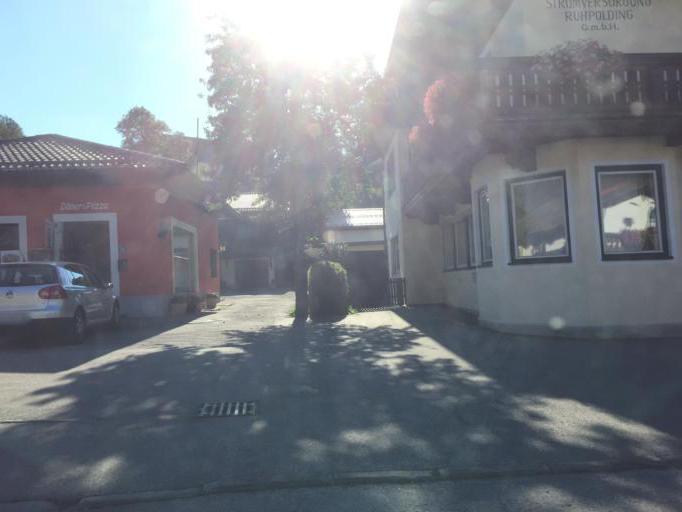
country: DE
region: Bavaria
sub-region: Upper Bavaria
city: Ruhpolding
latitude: 47.7630
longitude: 12.6446
